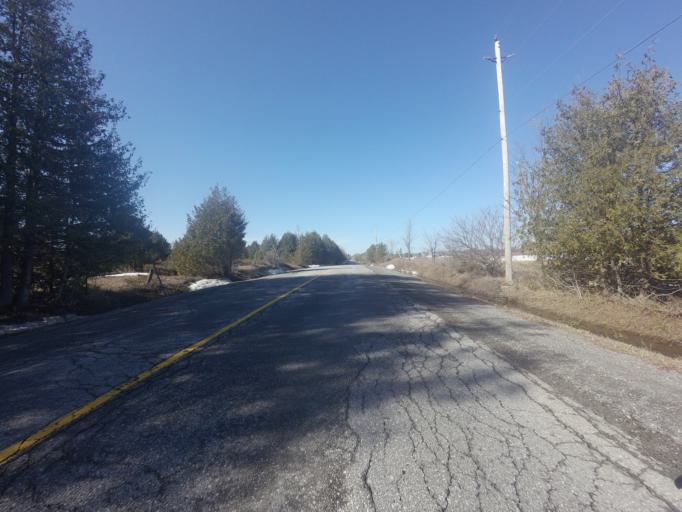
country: CA
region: Ontario
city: Carleton Place
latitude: 45.2006
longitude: -75.9885
